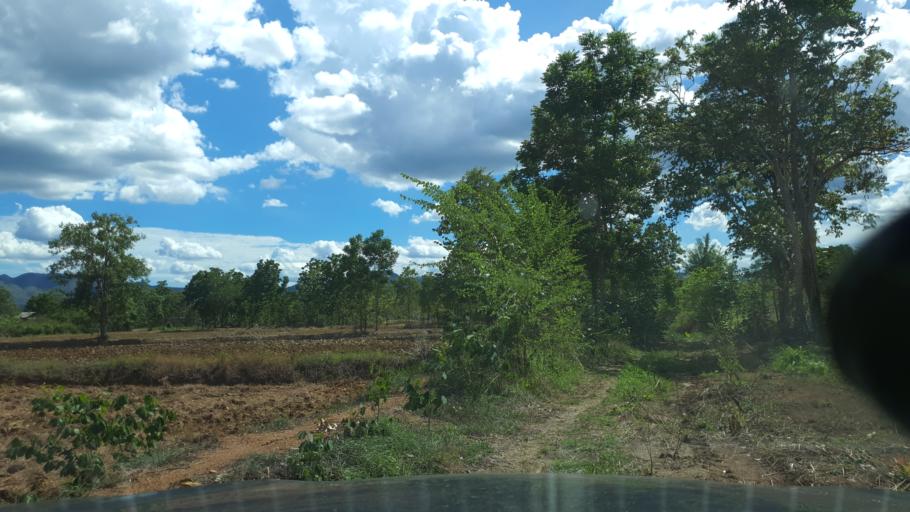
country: TH
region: Sukhothai
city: Thung Saliam
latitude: 17.3410
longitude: 99.4364
